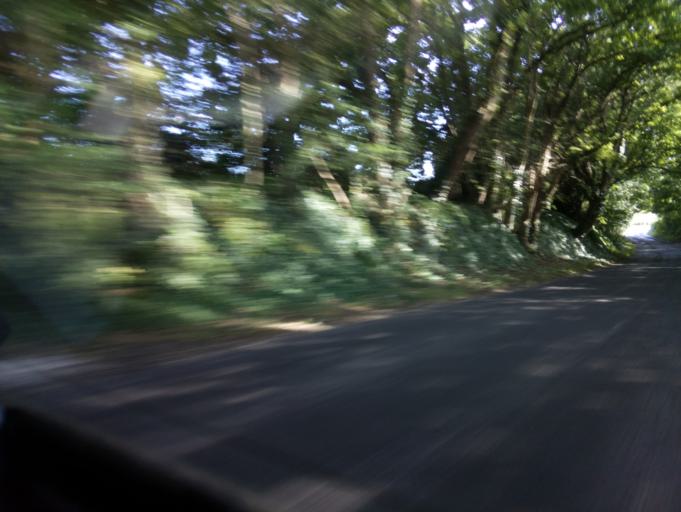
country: GB
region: England
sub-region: Hampshire
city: Chandlers Ford
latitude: 50.9844
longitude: -1.4320
